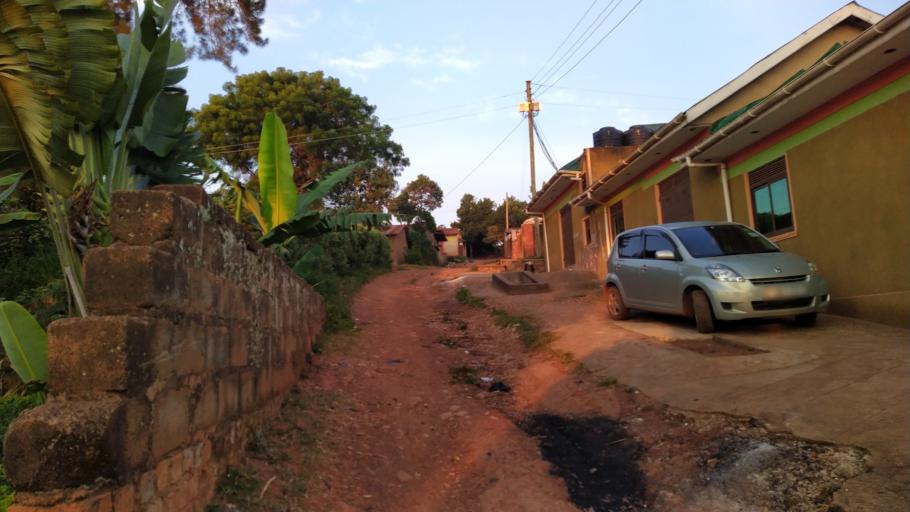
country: UG
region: Central Region
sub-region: Kampala District
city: Kampala
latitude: 0.2704
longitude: 32.5742
